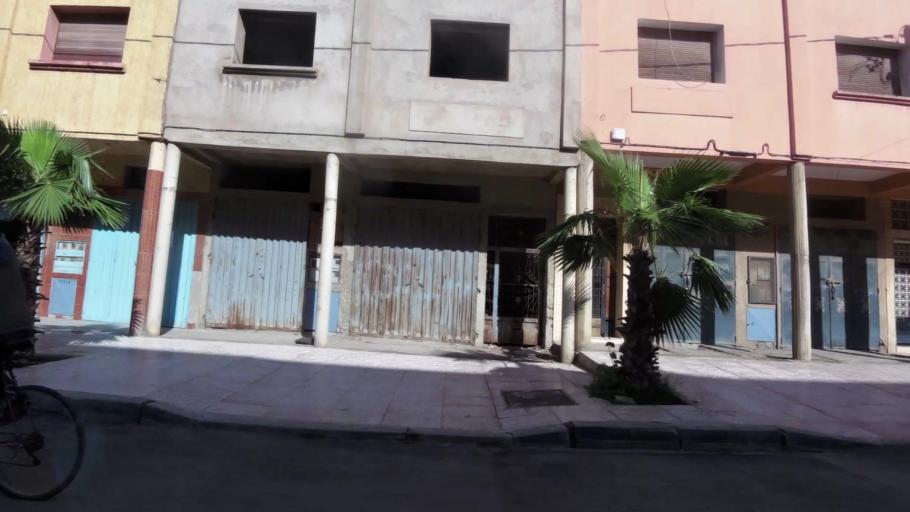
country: MA
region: Chaouia-Ouardigha
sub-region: Settat Province
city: Berrechid
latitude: 33.2604
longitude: -7.5719
